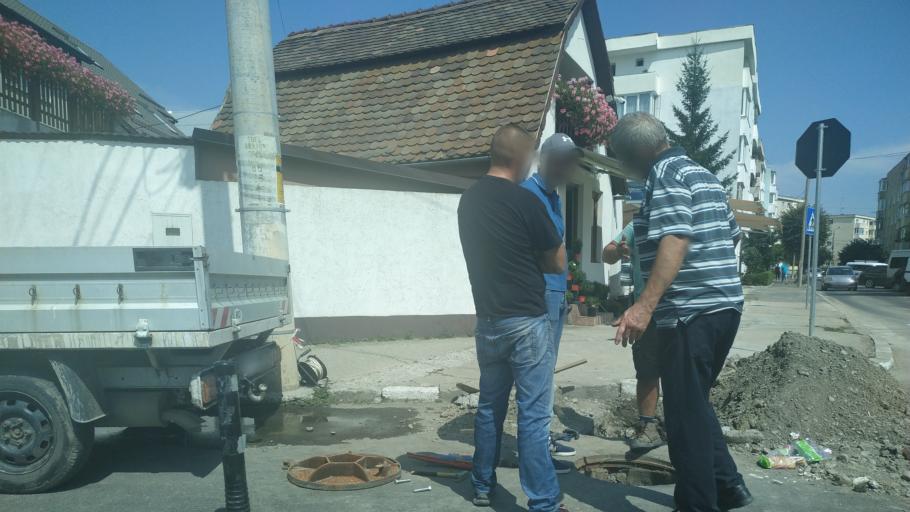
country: RO
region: Brasov
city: Fogarasch
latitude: 45.8410
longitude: 24.9661
